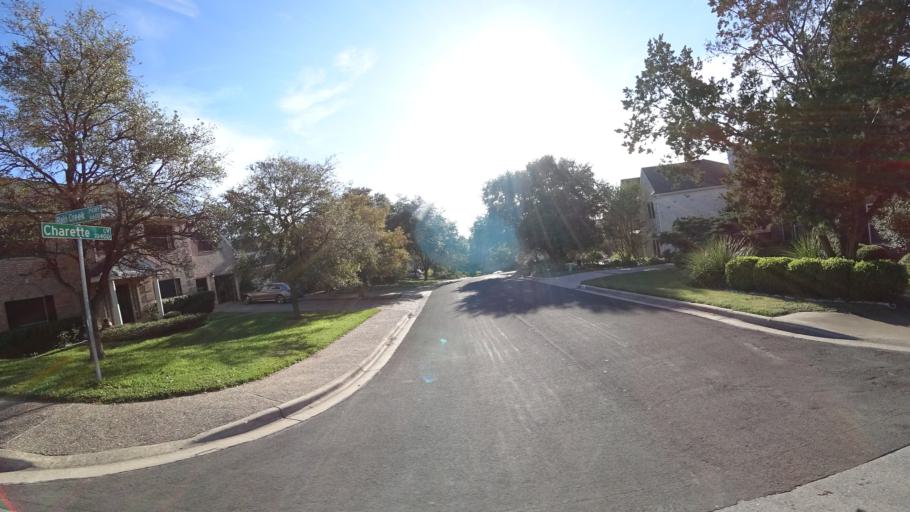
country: US
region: Texas
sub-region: Williamson County
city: Jollyville
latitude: 30.4114
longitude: -97.7698
